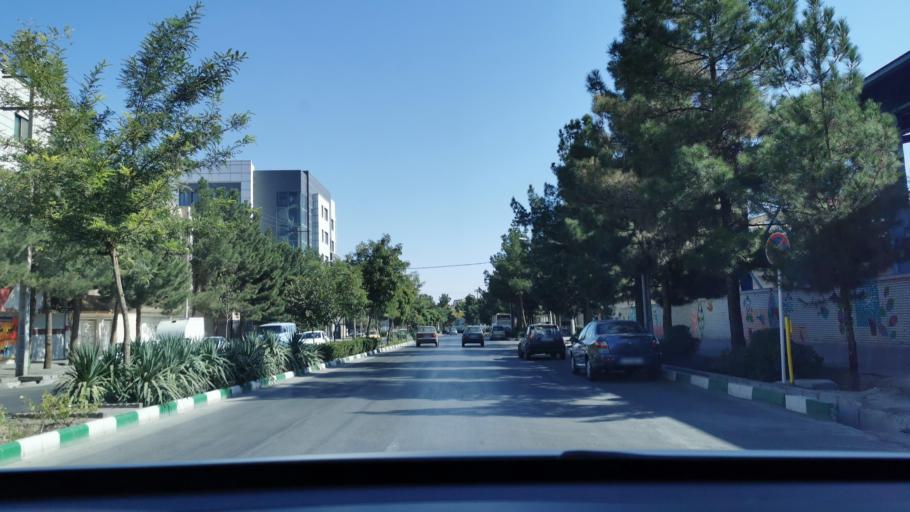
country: IR
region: Razavi Khorasan
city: Mashhad
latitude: 36.3347
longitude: 59.5928
